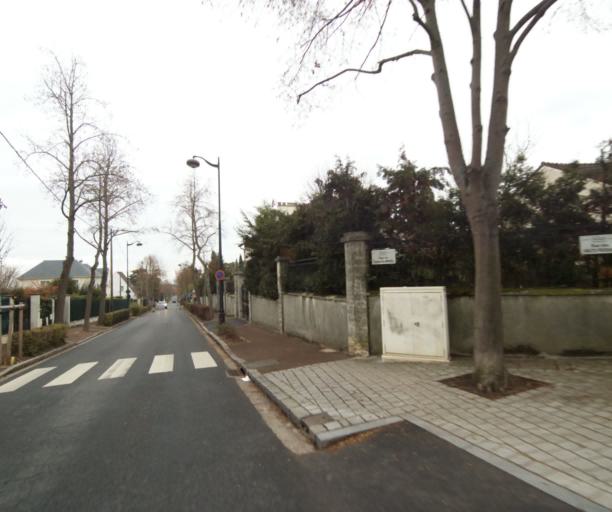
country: FR
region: Ile-de-France
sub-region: Departement des Hauts-de-Seine
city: Rueil-Malmaison
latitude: 48.8633
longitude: 2.1716
